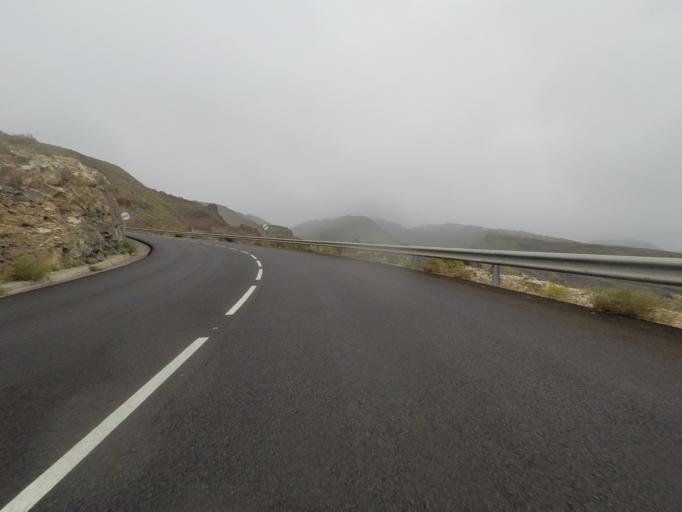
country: ES
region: Canary Islands
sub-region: Provincia de Santa Cruz de Tenerife
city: Alajero
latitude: 28.0538
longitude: -17.1996
